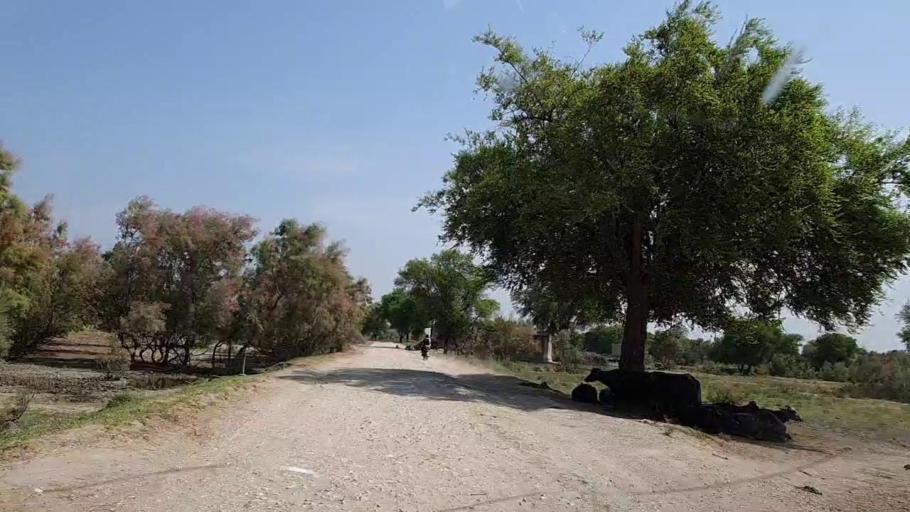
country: PK
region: Sindh
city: Khanpur
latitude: 27.8181
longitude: 69.3054
